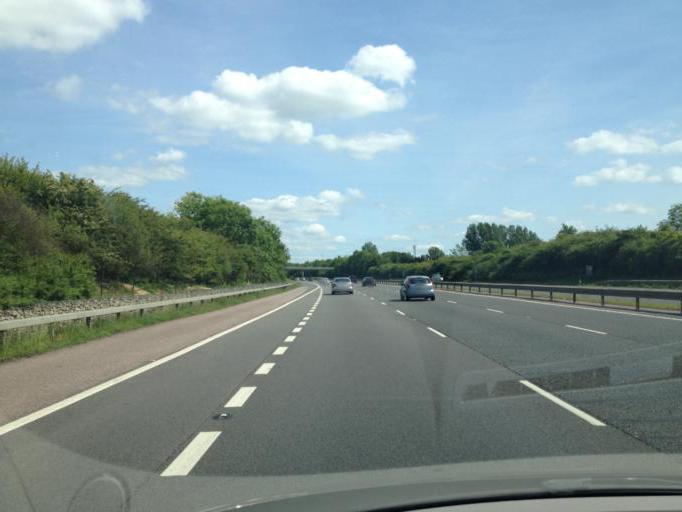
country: GB
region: England
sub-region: Oxfordshire
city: Wheatley
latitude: 51.7376
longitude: -1.0916
